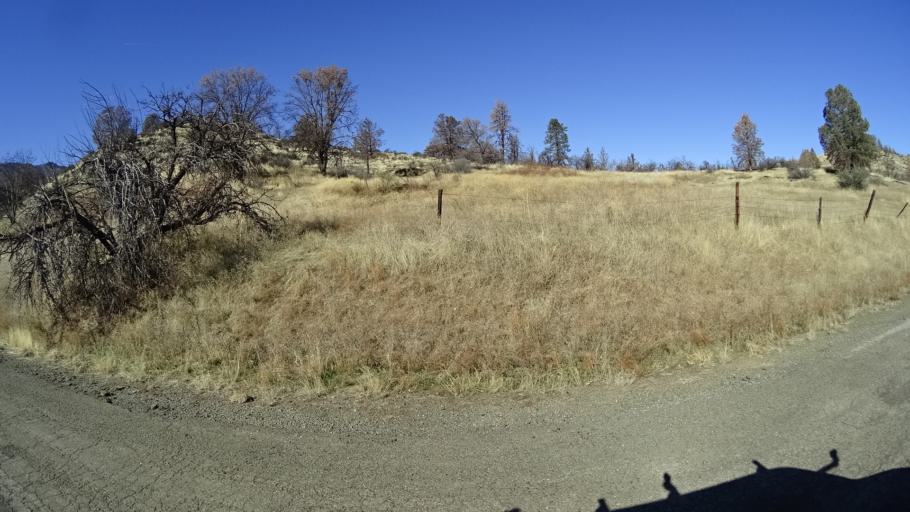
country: US
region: California
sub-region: Siskiyou County
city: Montague
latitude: 41.8885
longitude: -122.5523
